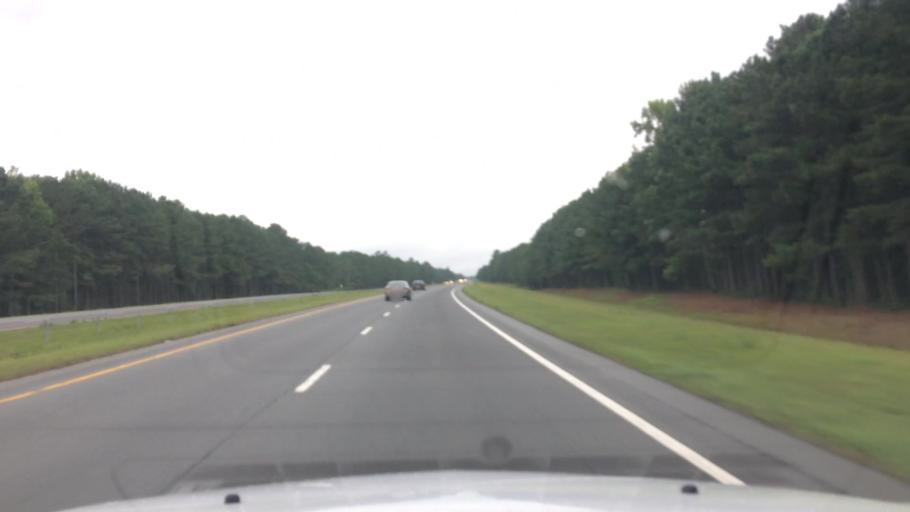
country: US
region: North Carolina
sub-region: Pitt County
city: Farmville
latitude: 35.6266
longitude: -77.7129
